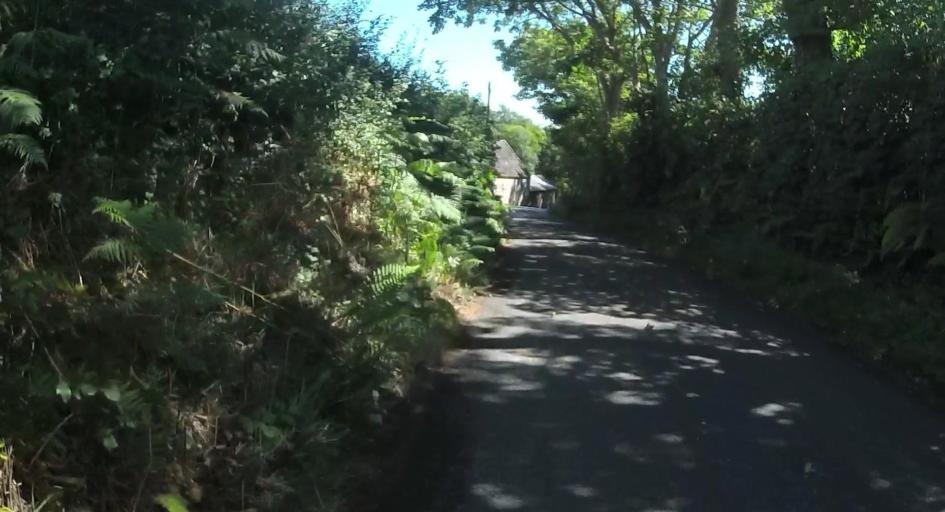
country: GB
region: England
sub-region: Isle of Wight
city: Niton
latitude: 50.6150
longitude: -1.2847
